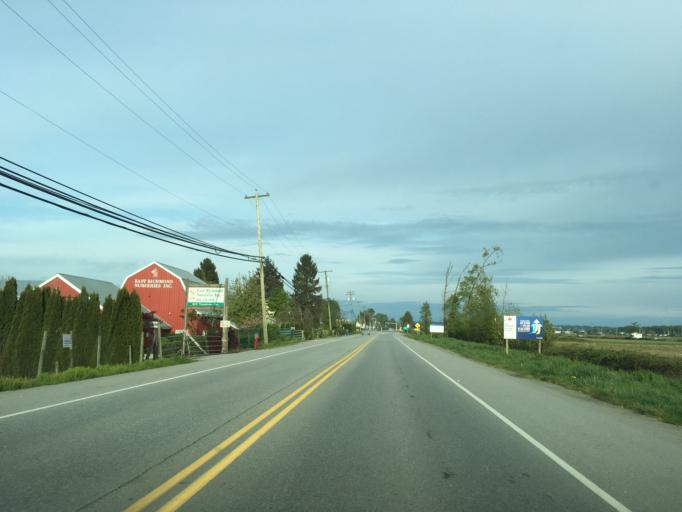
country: CA
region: British Columbia
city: Ladner
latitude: 49.1699
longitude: -123.0212
